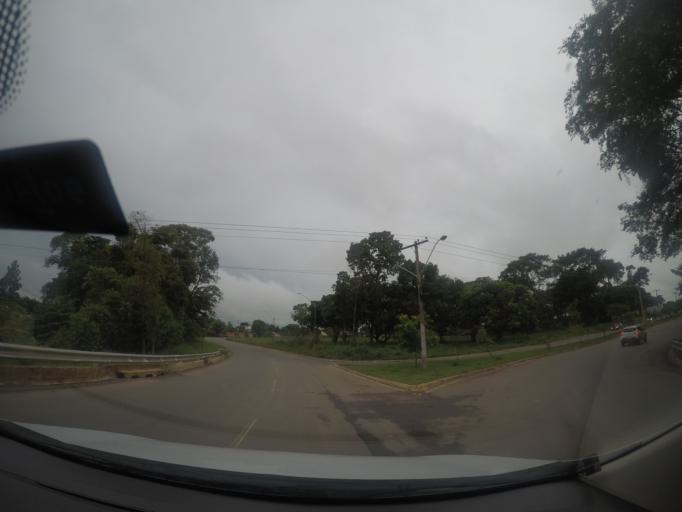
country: BR
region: Goias
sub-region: Aparecida De Goiania
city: Aparecida de Goiania
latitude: -16.7667
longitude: -49.3031
